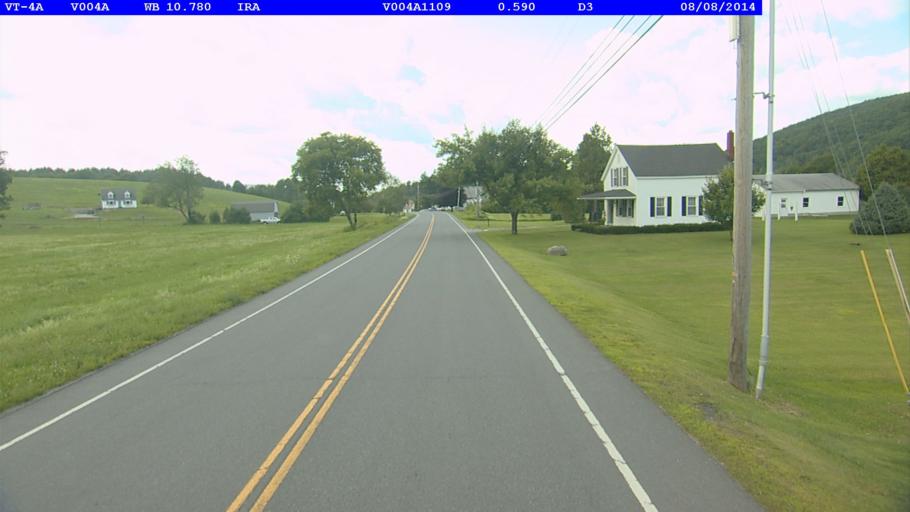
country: US
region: Vermont
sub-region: Rutland County
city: West Rutland
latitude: 43.6096
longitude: -73.1013
